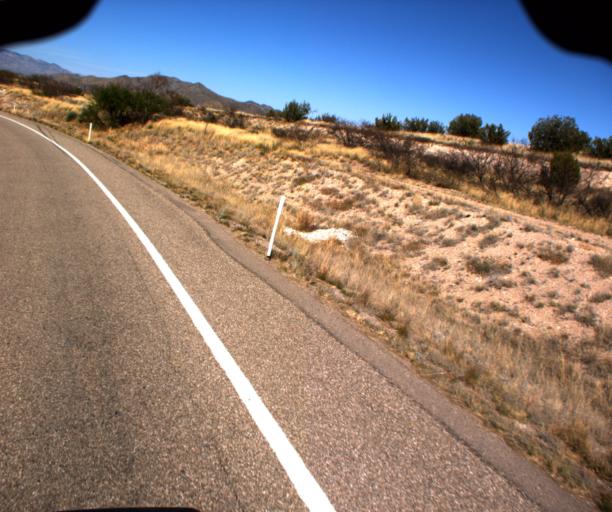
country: US
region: Arizona
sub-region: Pima County
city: Corona de Tucson
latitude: 31.8335
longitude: -110.7019
